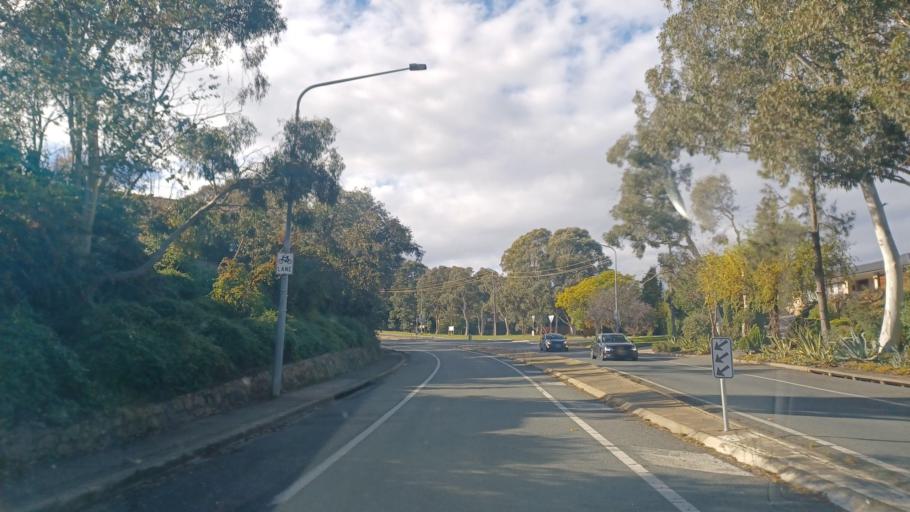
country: AU
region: Australian Capital Territory
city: Belconnen
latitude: -35.1997
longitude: 149.0439
